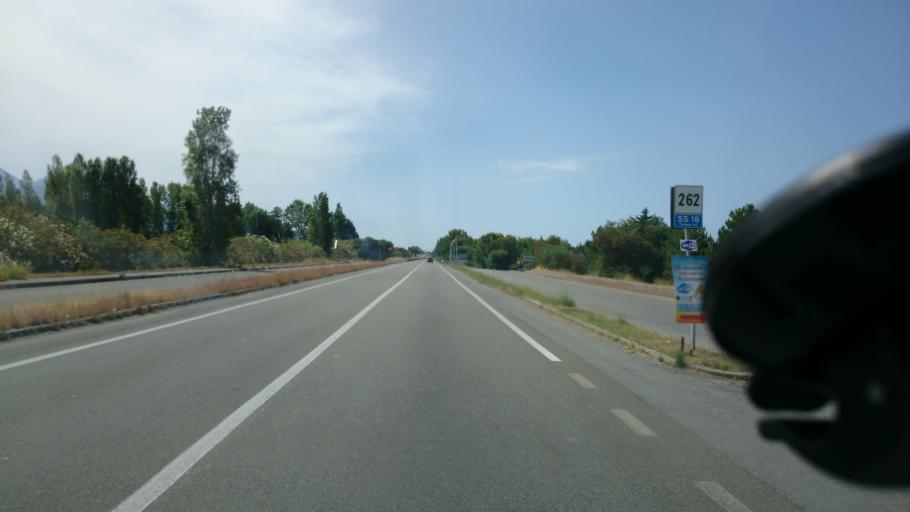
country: IT
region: Calabria
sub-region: Provincia di Cosenza
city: Scalea
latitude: 39.7935
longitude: 15.7933
